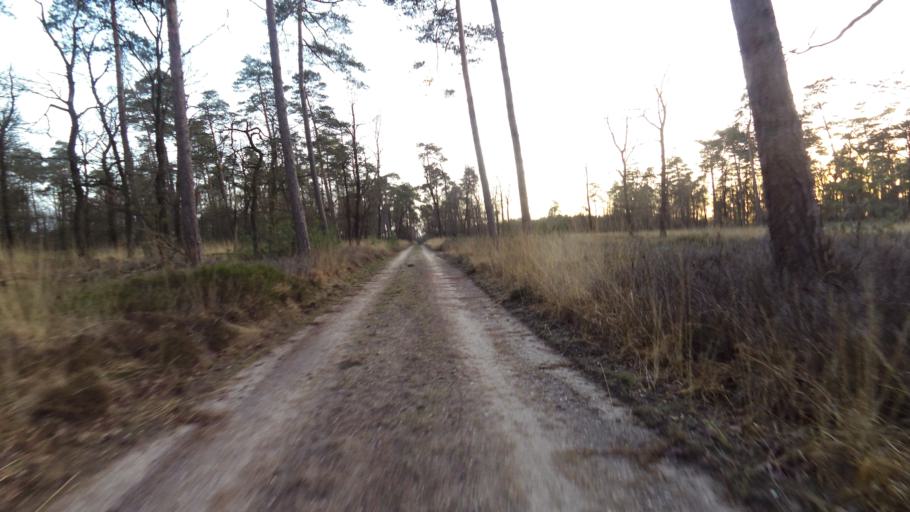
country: NL
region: Gelderland
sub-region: Gemeente Apeldoorn
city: Uddel
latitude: 52.2974
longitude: 5.8466
